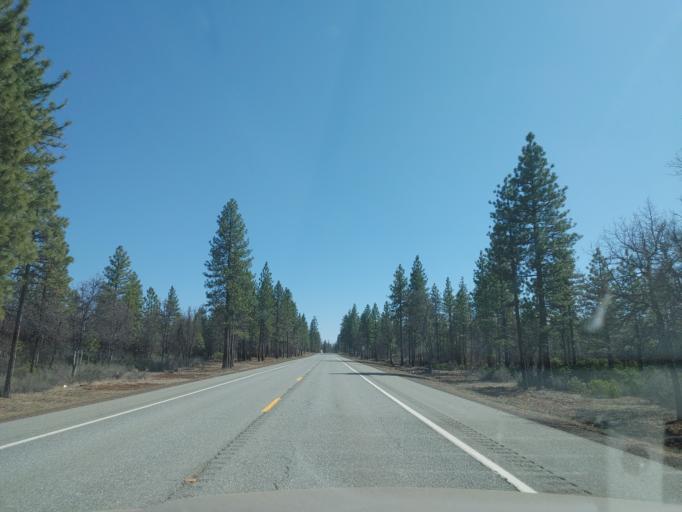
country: US
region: California
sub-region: Shasta County
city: Burney
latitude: 40.9451
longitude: -121.6094
